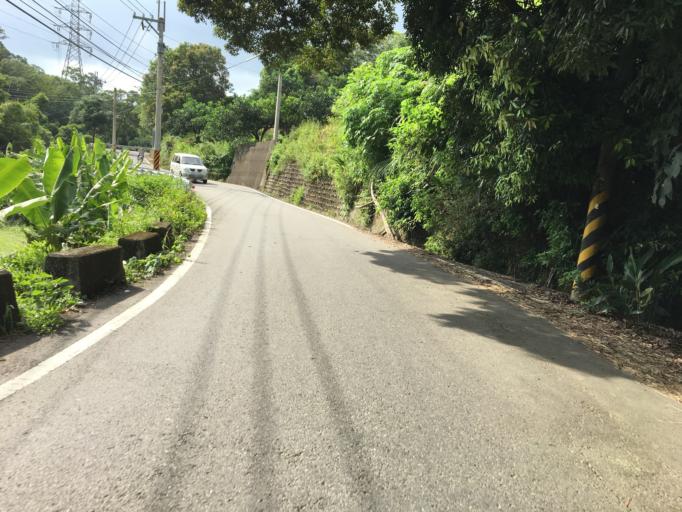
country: TW
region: Taiwan
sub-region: Hsinchu
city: Hsinchu
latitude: 24.7013
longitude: 120.9588
